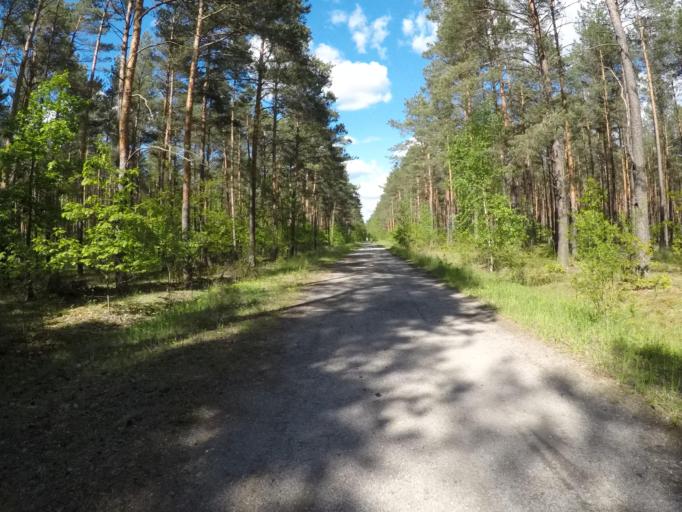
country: PL
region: Swietokrzyskie
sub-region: Powiat kielecki
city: Kostomloty Drugie
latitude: 50.8930
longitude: 20.5430
